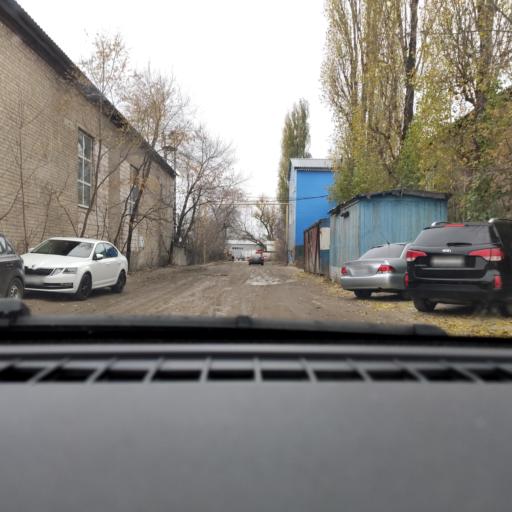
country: RU
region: Voronezj
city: Voronezh
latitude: 51.6237
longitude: 39.2293
